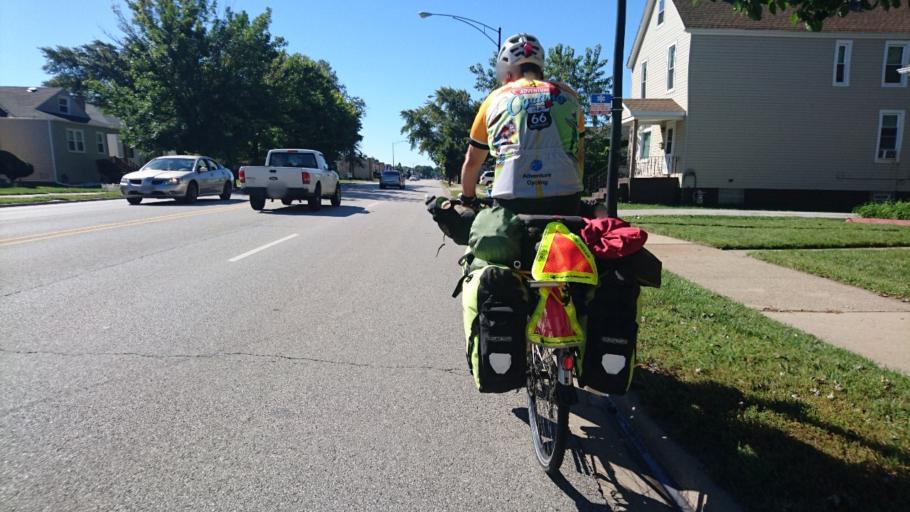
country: US
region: Illinois
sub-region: Cook County
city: Burnham
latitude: 41.6572
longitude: -87.5400
